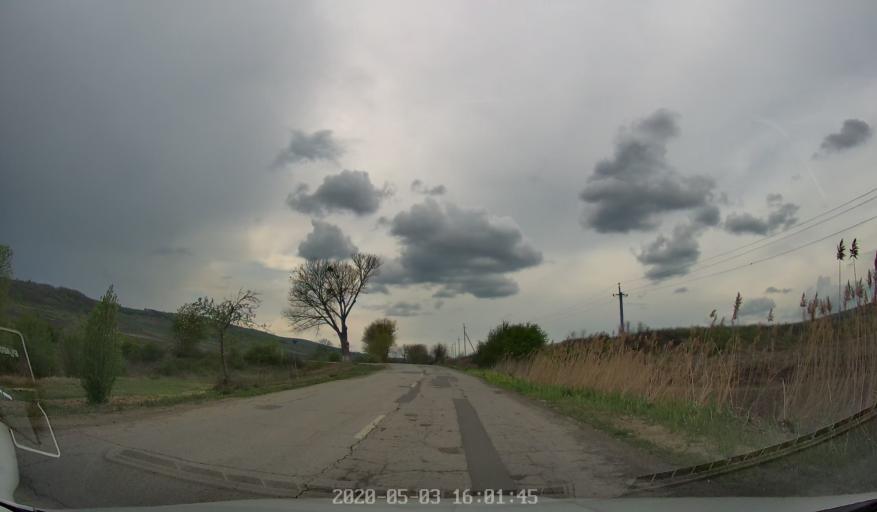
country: MD
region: Stinga Nistrului
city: Bucovat
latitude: 47.1688
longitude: 28.4051
